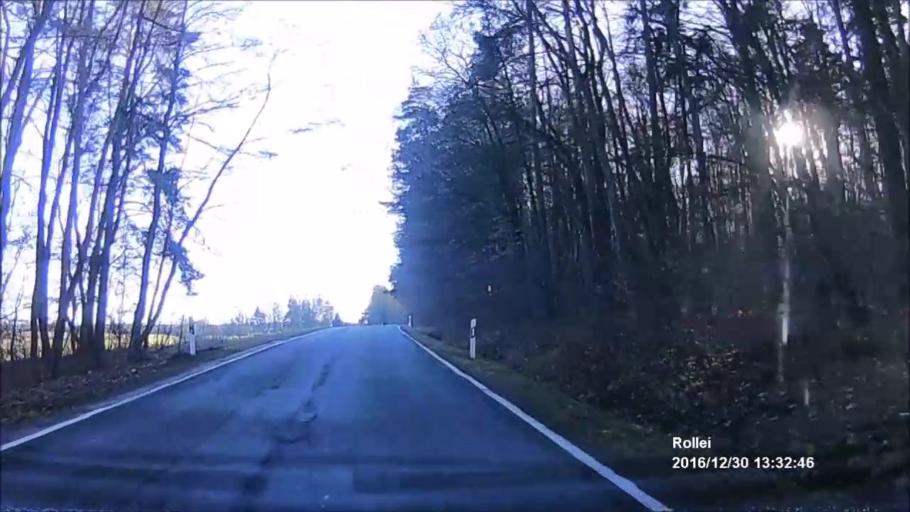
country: DE
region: Thuringia
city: Klettbach
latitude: 50.9261
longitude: 11.1075
